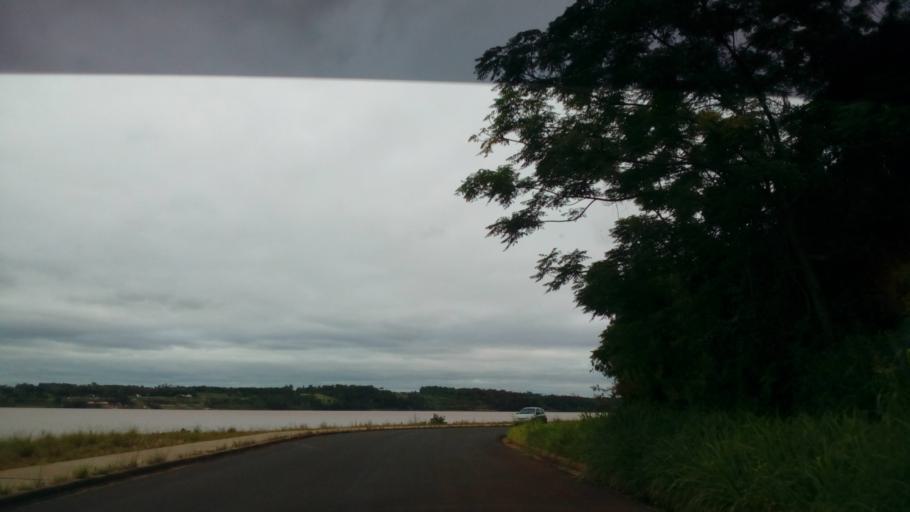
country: AR
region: Misiones
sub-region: Departamento de Candelaria
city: Candelaria
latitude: -27.4511
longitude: -55.7587
